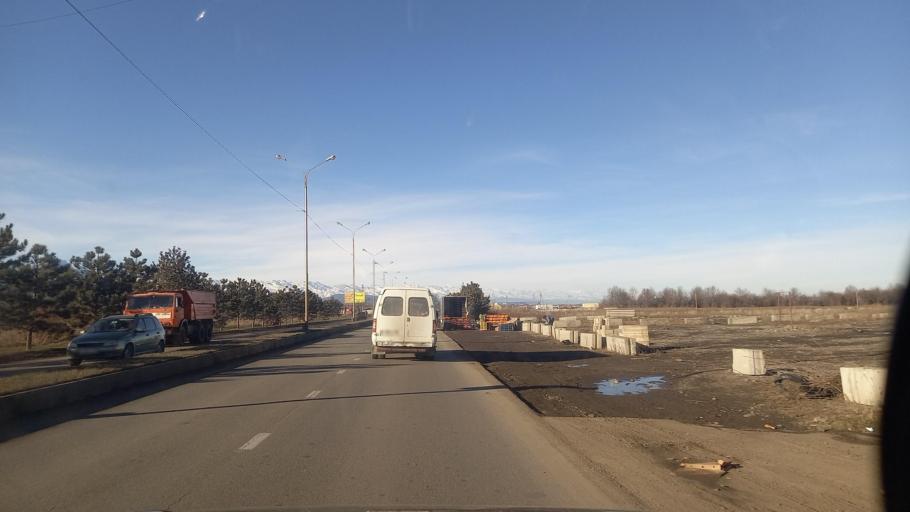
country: RU
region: North Ossetia
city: Vladikavkaz
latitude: 43.0254
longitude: 44.6305
